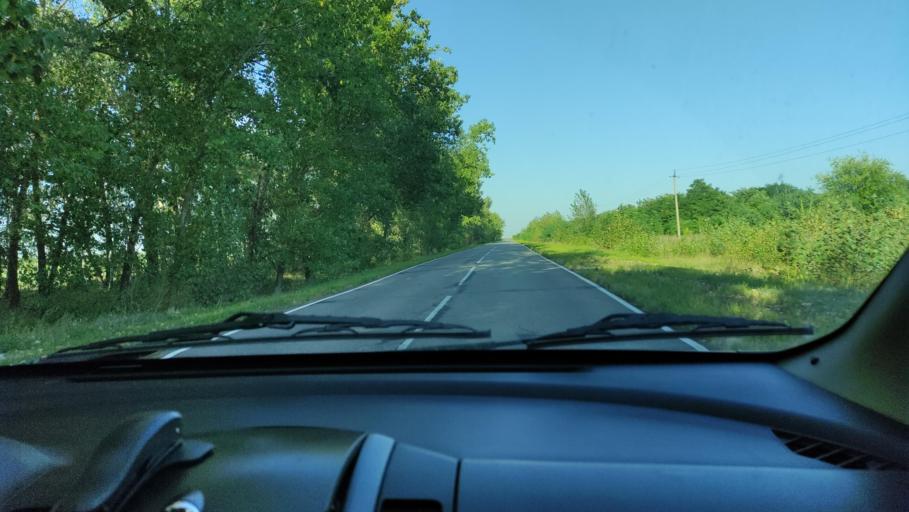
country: RU
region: Voronezj
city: Verkhniy Mamon
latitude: 50.1194
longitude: 40.2989
